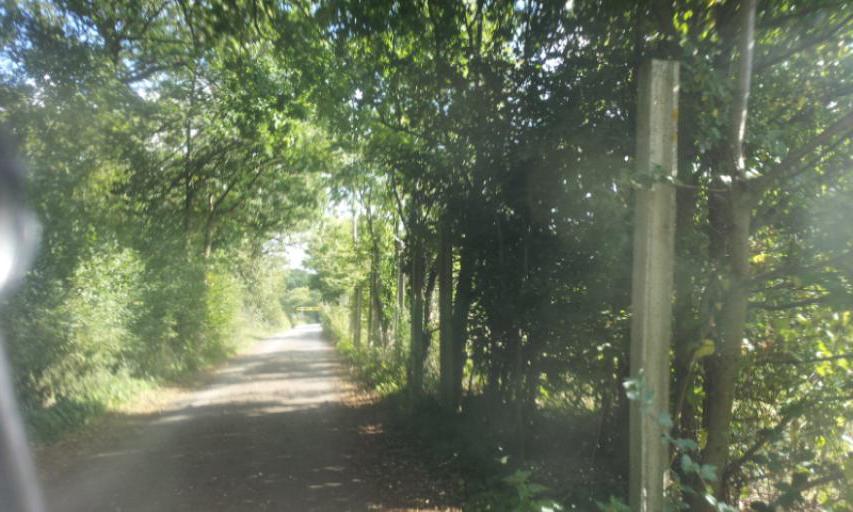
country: GB
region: England
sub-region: Greater London
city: Chislehurst
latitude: 51.3960
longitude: 0.0606
